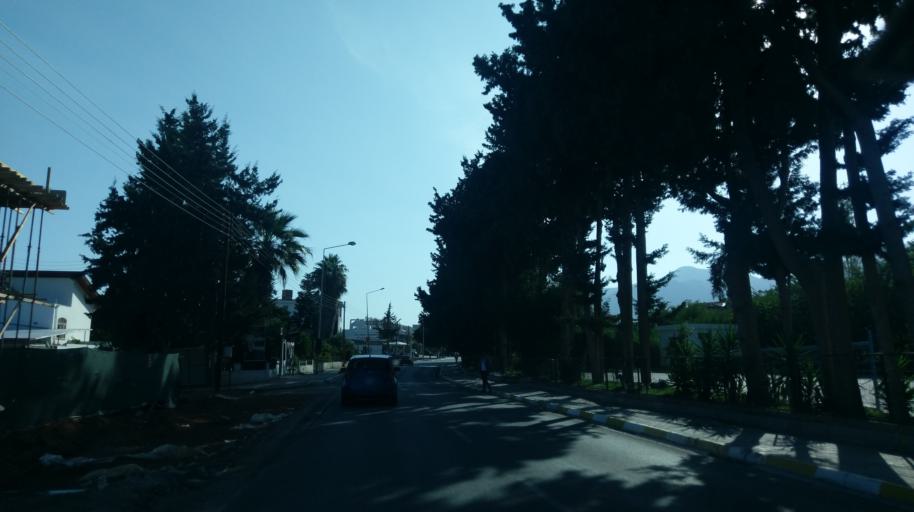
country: CY
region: Keryneia
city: Kyrenia
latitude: 35.3316
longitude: 33.3322
